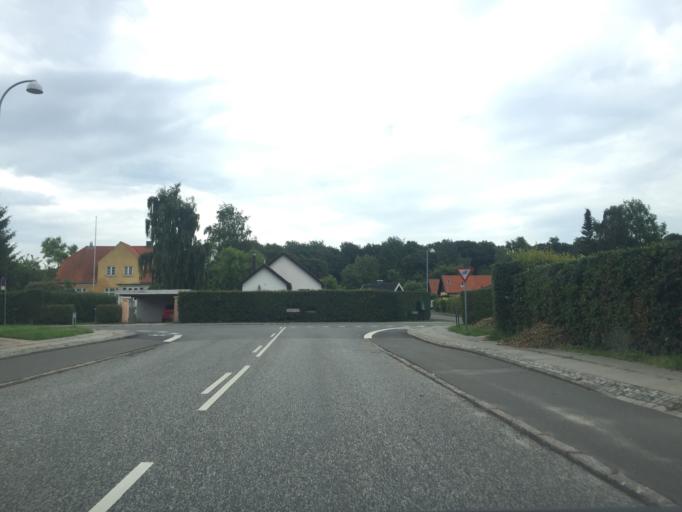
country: DK
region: Capital Region
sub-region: Lyngby-Tarbaek Kommune
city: Kongens Lyngby
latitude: 55.7948
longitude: 12.5412
